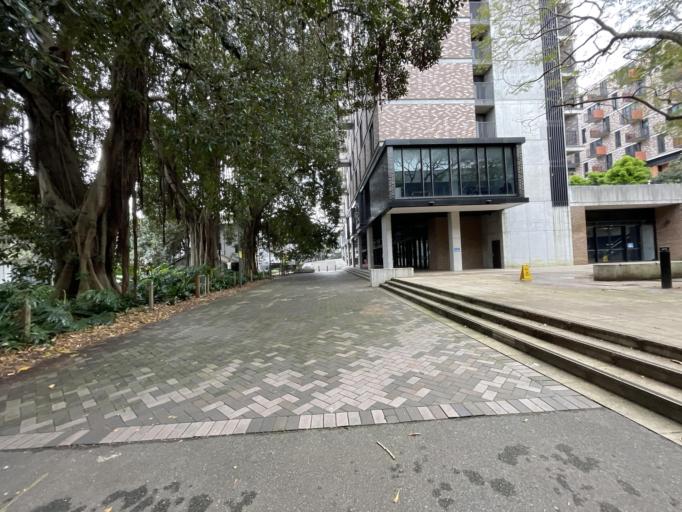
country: AU
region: New South Wales
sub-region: Randwick
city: Kingsford
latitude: -33.9164
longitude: 151.2312
